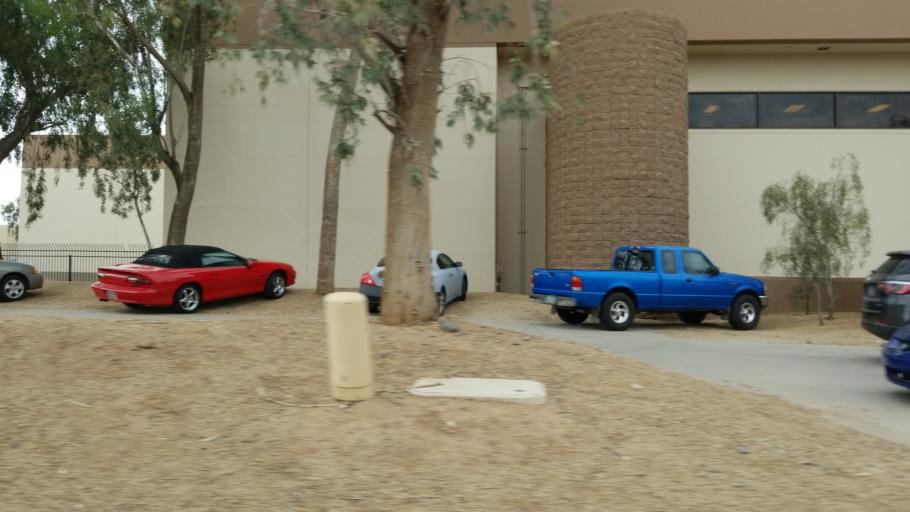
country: US
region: Arizona
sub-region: Maricopa County
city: Phoenix
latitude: 33.4477
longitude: -112.1501
